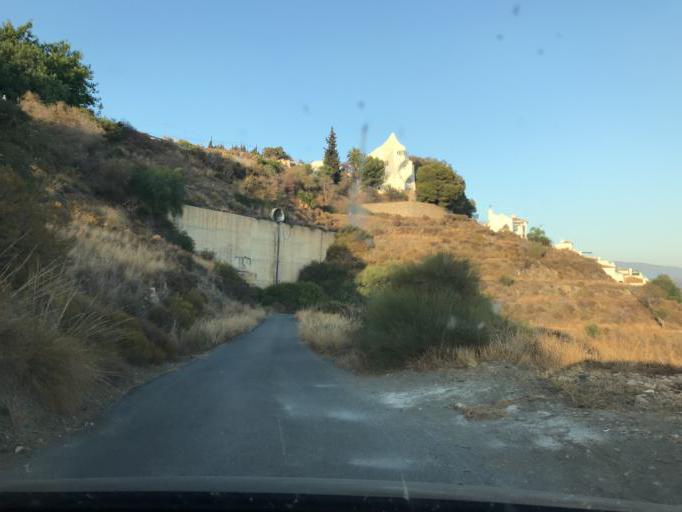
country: ES
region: Andalusia
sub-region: Provincia de Granada
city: Salobrena
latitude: 36.7431
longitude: -3.6181
